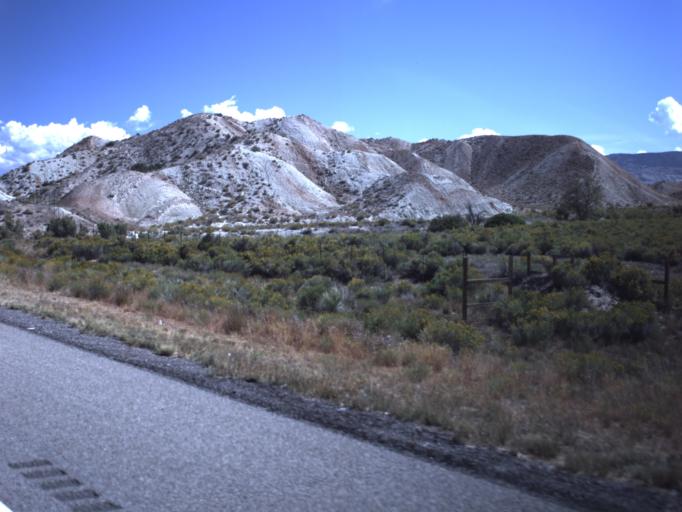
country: US
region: Utah
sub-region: Sevier County
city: Aurora
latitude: 38.9048
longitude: -111.9010
